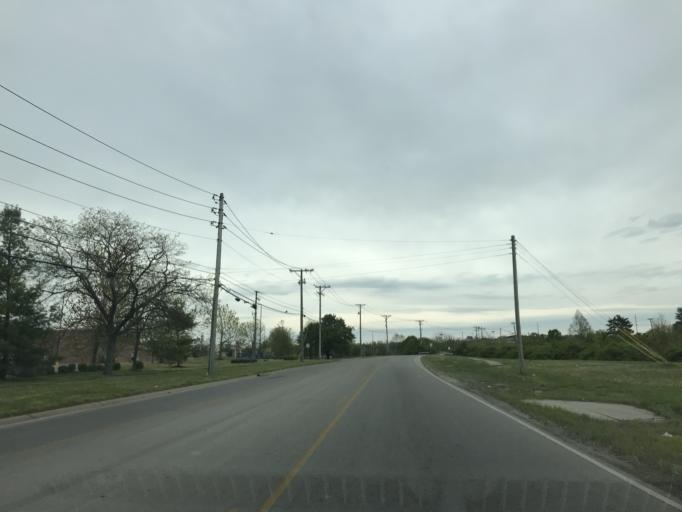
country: US
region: Kentucky
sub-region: Jefferson County
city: West Buechel
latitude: 38.1977
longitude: -85.6681
